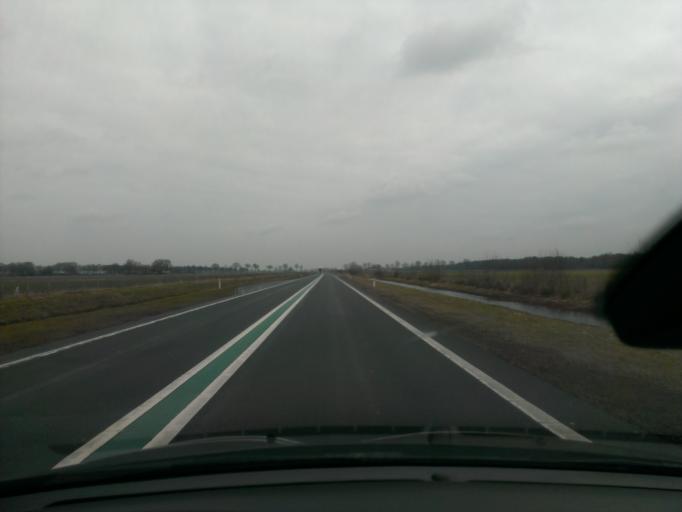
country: NL
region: Overijssel
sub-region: Gemeente Twenterand
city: Den Ham
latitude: 52.5510
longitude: 6.4412
